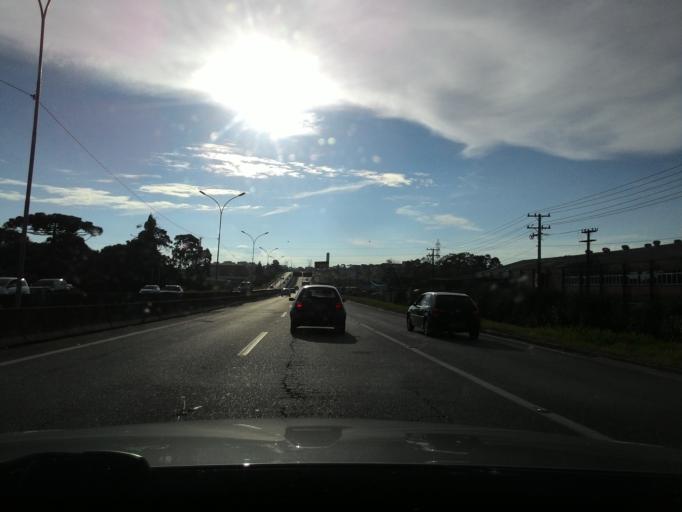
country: BR
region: Parana
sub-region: Pinhais
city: Pinhais
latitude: -25.3890
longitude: -49.1918
